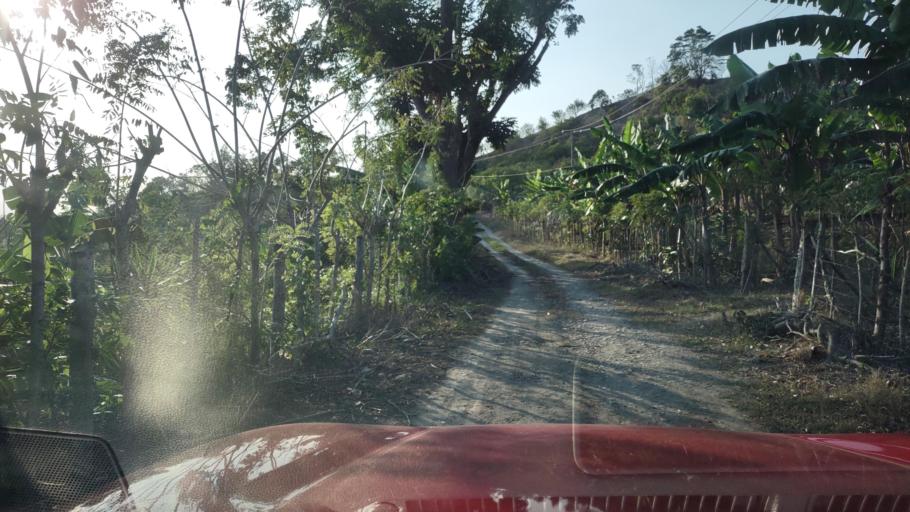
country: MX
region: Veracruz
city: Papantla de Olarte
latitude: 20.4601
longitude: -97.3693
